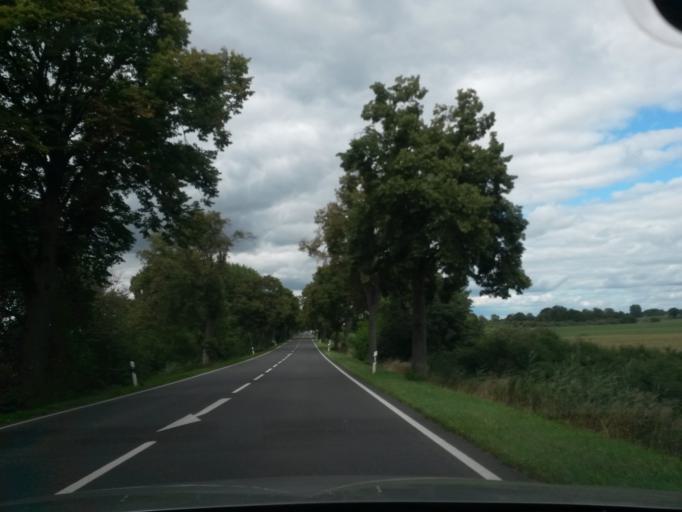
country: DE
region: Brandenburg
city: Angermunde
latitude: 52.9731
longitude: 13.9676
